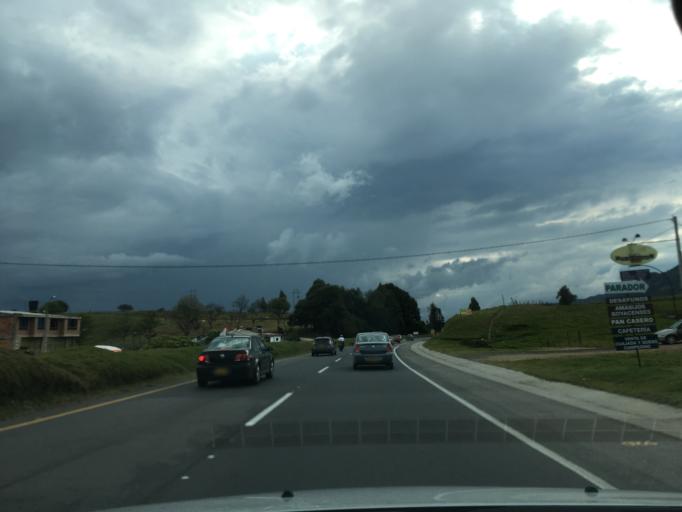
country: CO
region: Boyaca
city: Ventaquemada
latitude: 5.3993
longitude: -73.4823
